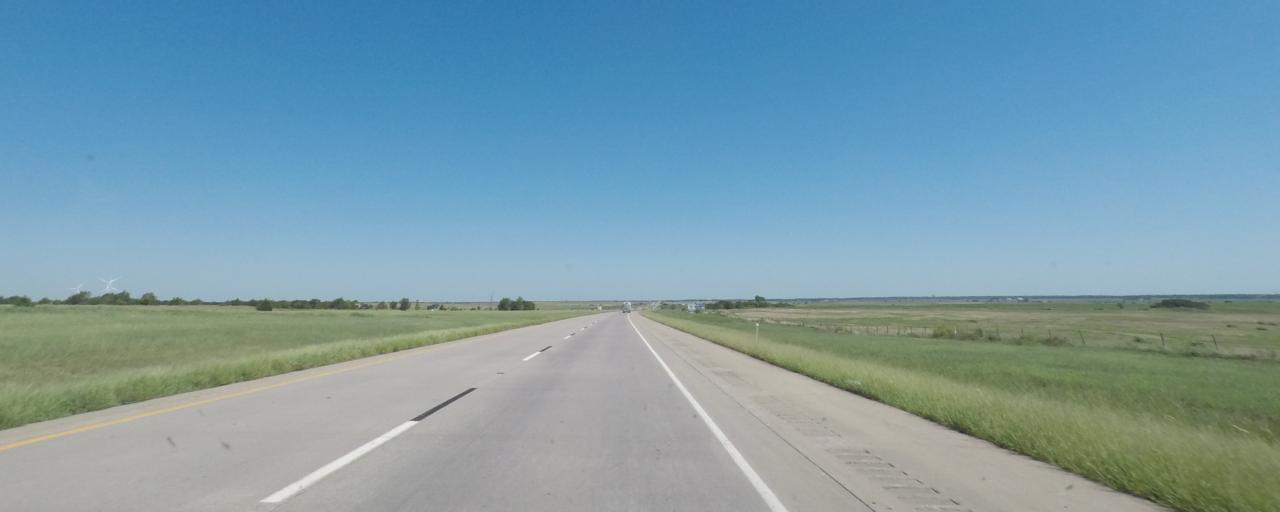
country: US
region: Oklahoma
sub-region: Kay County
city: Tonkawa
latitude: 36.5971
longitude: -97.3454
